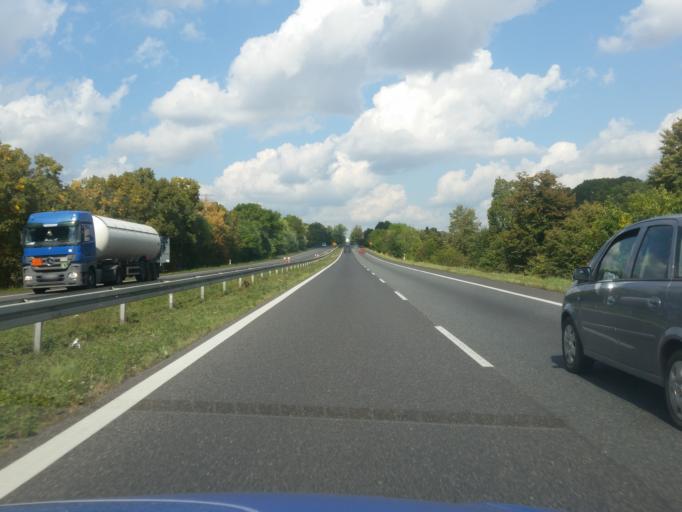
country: PL
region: Silesian Voivodeship
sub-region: Powiat bedzinski
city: Bedzin
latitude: 50.3435
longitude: 19.1103
